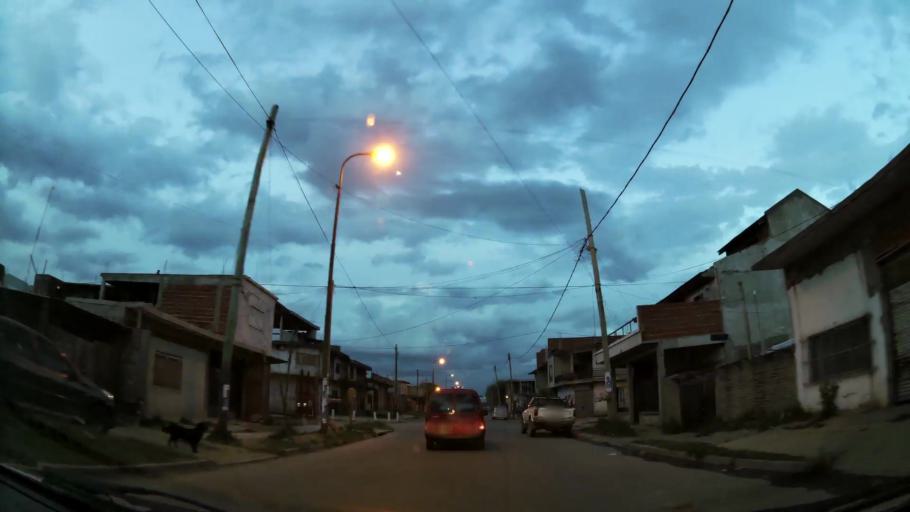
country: AR
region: Buenos Aires
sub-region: Partido de Quilmes
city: Quilmes
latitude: -34.7202
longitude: -58.2362
